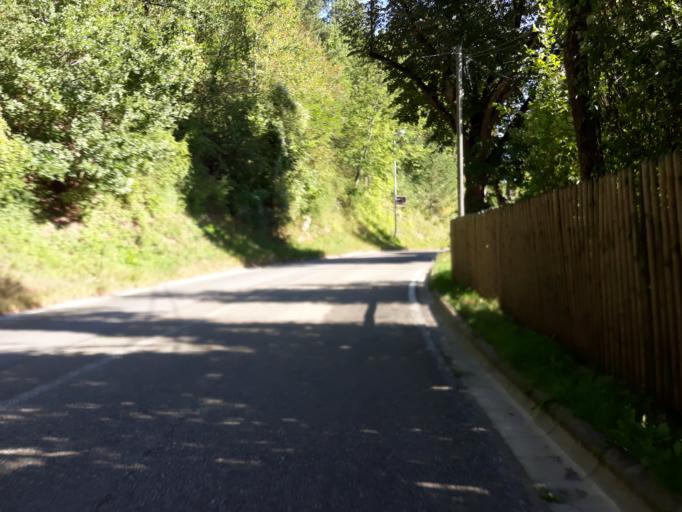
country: DE
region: Baden-Wuerttemberg
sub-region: Regierungsbezirk Stuttgart
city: Ehningen
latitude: 48.6611
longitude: 8.9275
